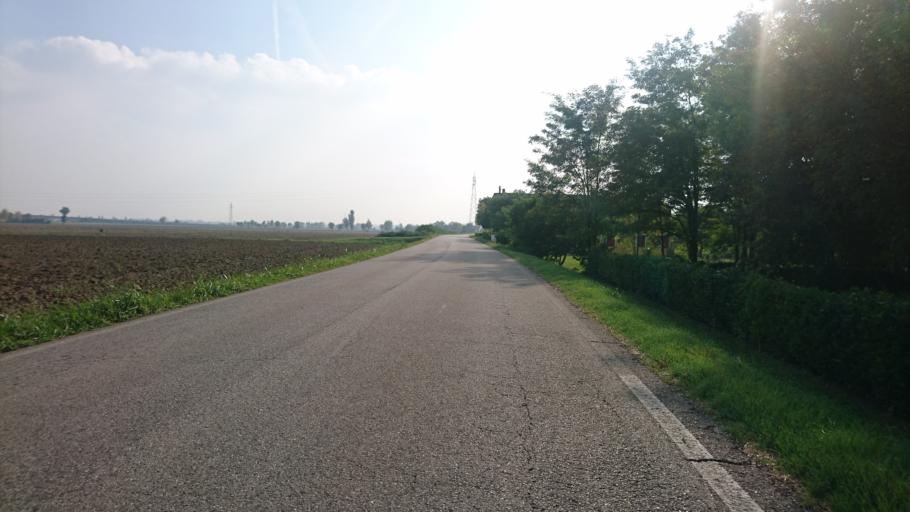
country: IT
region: Veneto
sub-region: Provincia di Rovigo
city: Grignano Polesine
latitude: 45.0336
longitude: 11.7516
